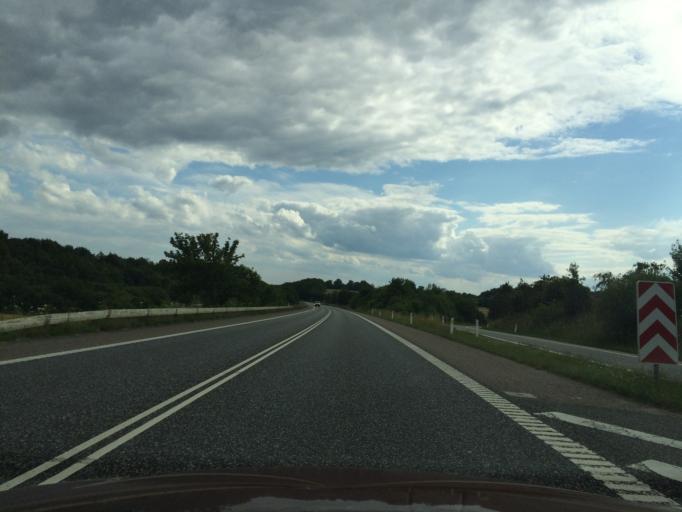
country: DK
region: Central Jutland
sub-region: Syddjurs Kommune
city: Hornslet
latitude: 56.2922
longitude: 10.3339
